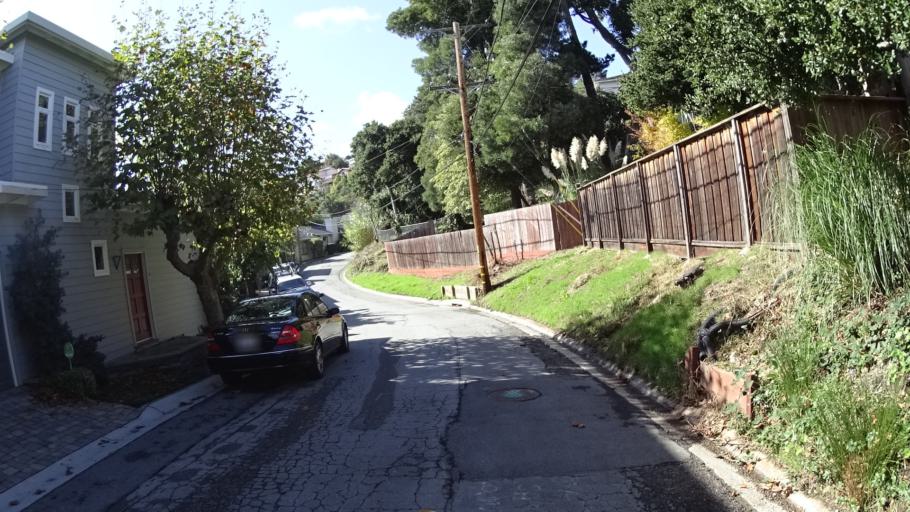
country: US
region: California
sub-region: San Mateo County
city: Millbrae
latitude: 37.5931
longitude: -122.4037
